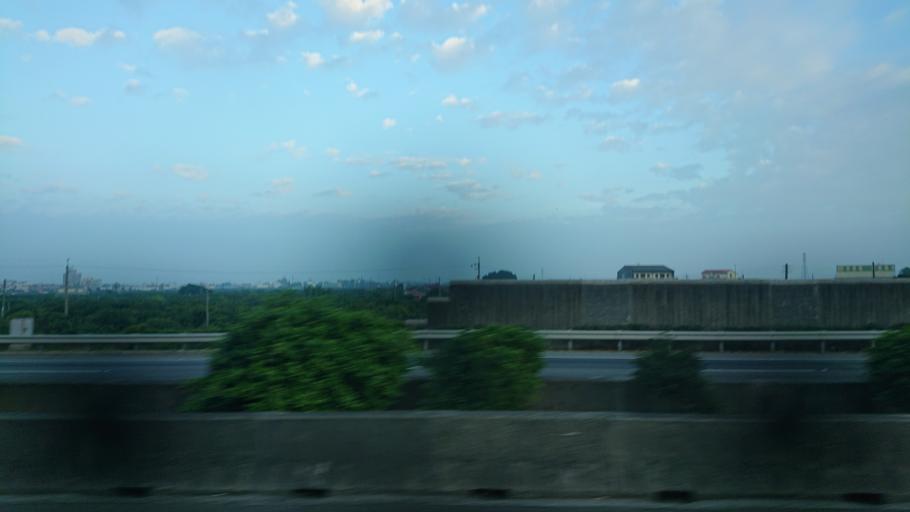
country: TW
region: Taiwan
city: Xinying
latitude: 23.1732
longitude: 120.2338
